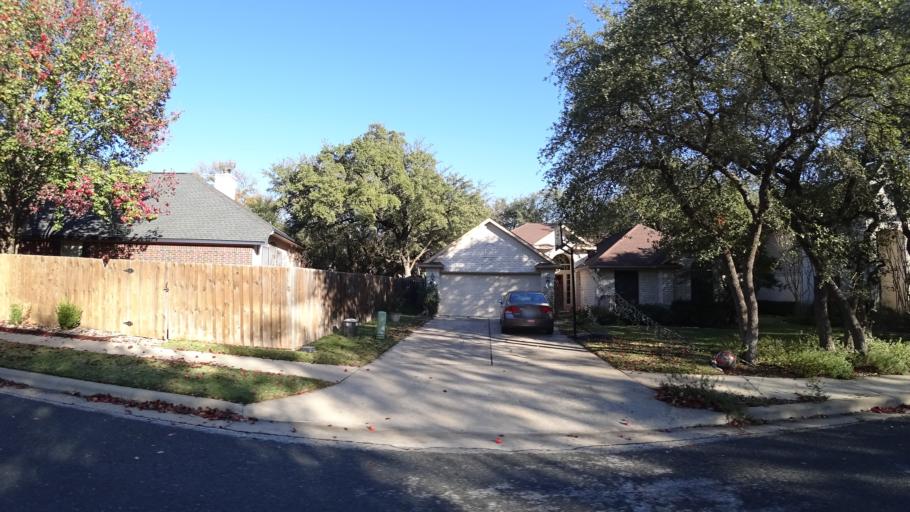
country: US
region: Texas
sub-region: Williamson County
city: Brushy Creek
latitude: 30.4947
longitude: -97.7454
